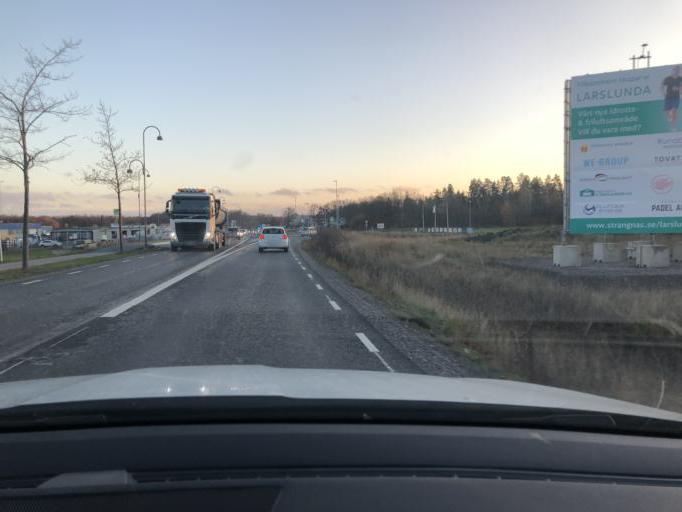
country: SE
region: Soedermanland
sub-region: Strangnas Kommun
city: Strangnas
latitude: 59.3551
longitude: 17.0283
